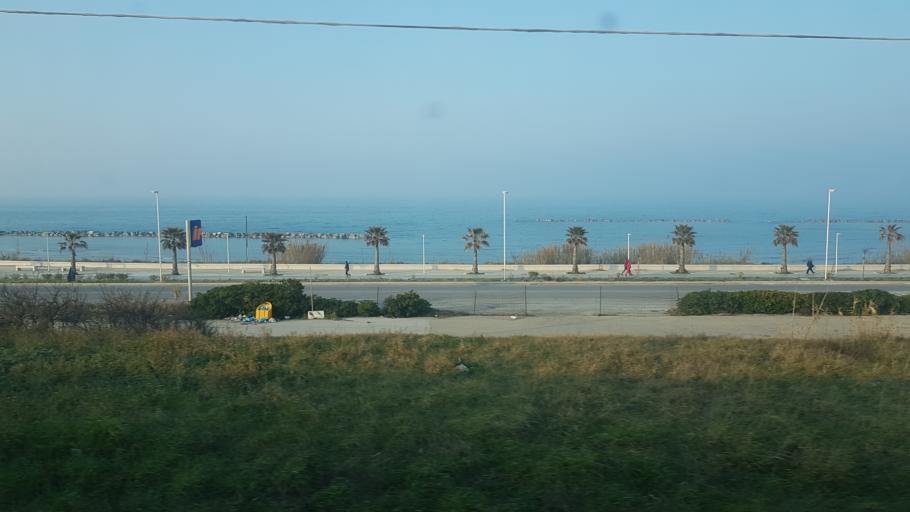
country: IT
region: Molise
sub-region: Provincia di Campobasso
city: Termoli
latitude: 42.0075
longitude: 14.9637
